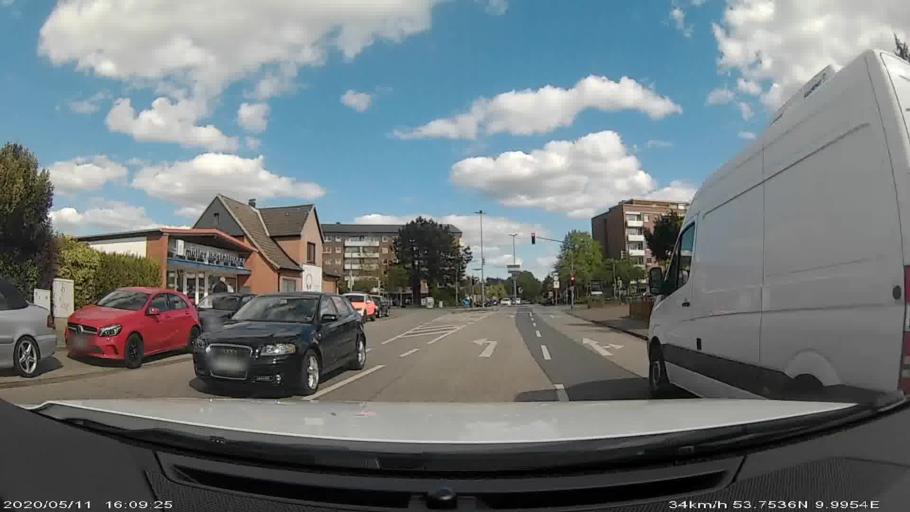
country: DE
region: Schleswig-Holstein
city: Henstedt-Ulzburg
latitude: 53.7515
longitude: 10.0036
